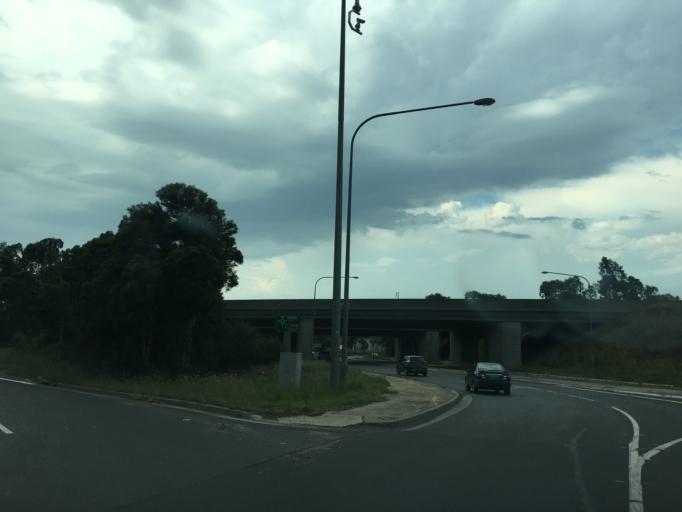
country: AU
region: New South Wales
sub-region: Liverpool
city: Miller
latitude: -33.9342
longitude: 150.8687
